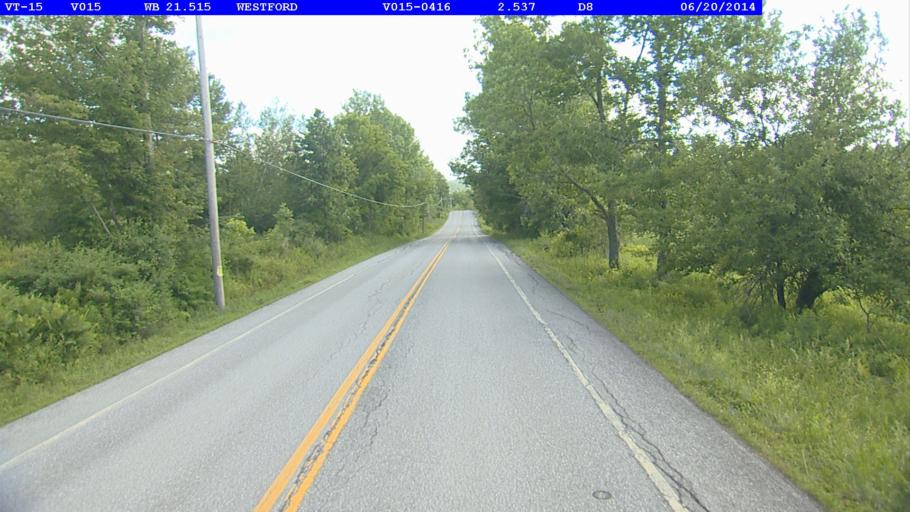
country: US
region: Vermont
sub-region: Chittenden County
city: Jericho
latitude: 44.6282
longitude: -72.9193
